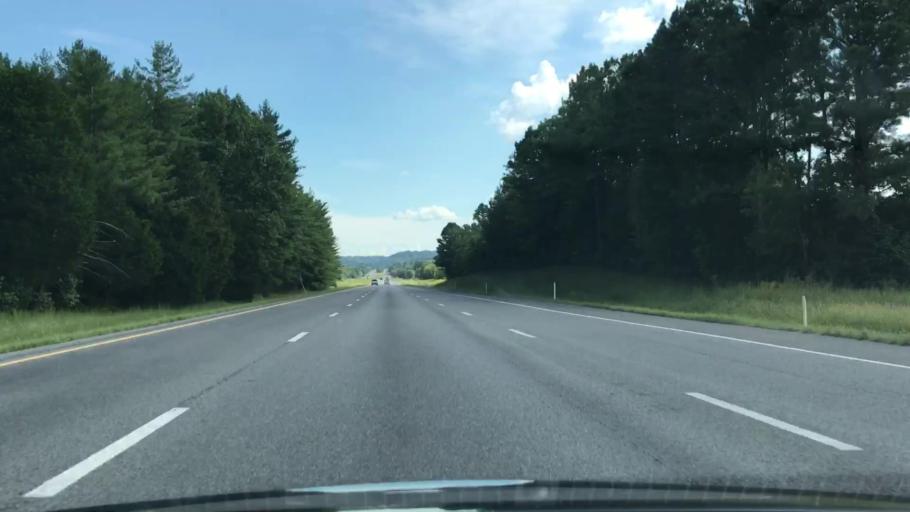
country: US
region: Tennessee
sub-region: Marshall County
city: Lewisburg
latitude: 35.4455
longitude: -86.8835
